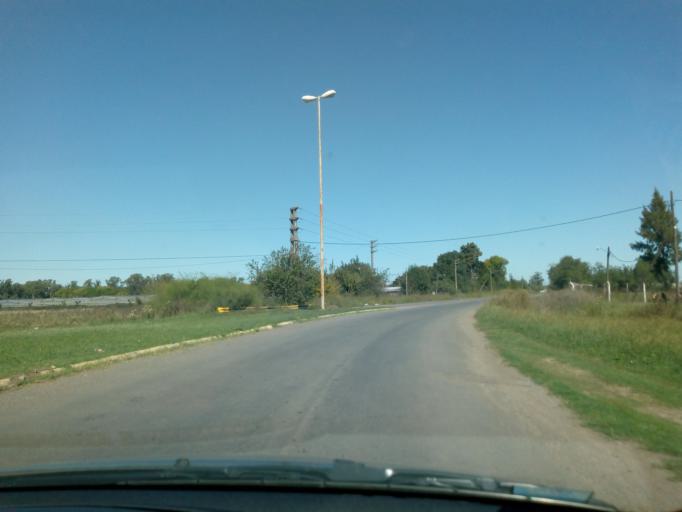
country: AR
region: Buenos Aires
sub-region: Partido de La Plata
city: La Plata
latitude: -35.0054
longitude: -58.0223
